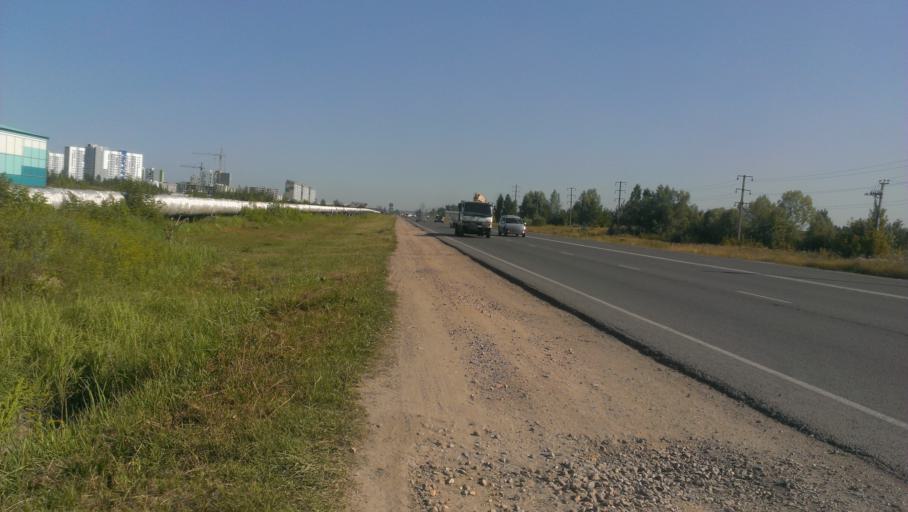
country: RU
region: Altai Krai
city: Novosilikatnyy
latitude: 53.3466
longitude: 83.6325
